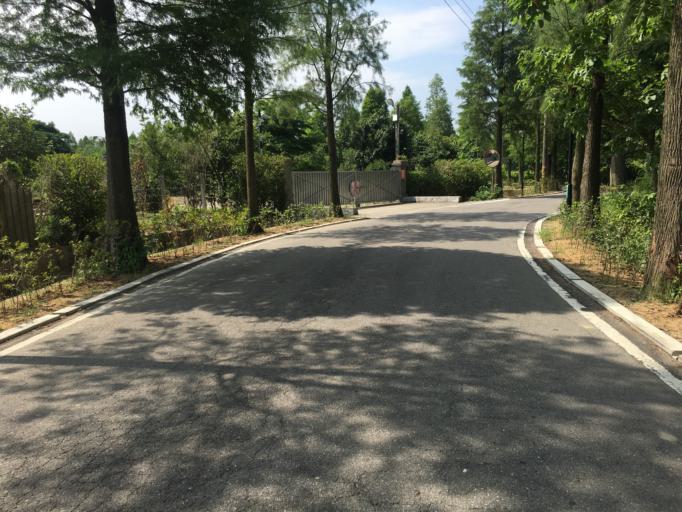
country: TW
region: Taiwan
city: Daxi
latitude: 24.8750
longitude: 121.2549
